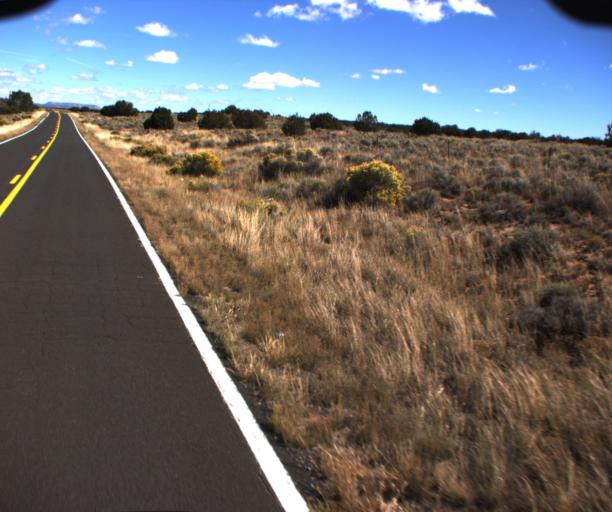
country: US
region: New Mexico
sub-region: McKinley County
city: Zuni Pueblo
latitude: 34.9948
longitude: -109.0973
